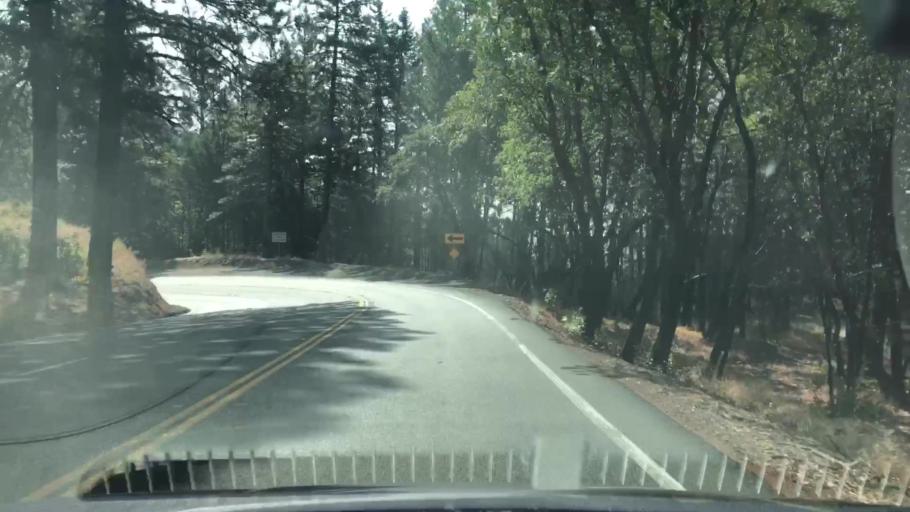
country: US
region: California
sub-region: Napa County
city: Calistoga
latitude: 38.6490
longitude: -122.5969
